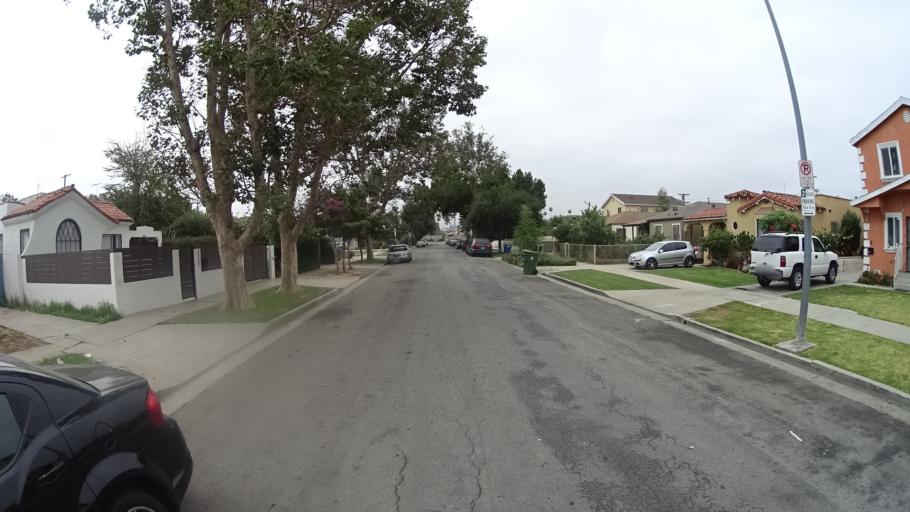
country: US
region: California
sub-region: Los Angeles County
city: View Park-Windsor Hills
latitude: 34.0246
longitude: -118.3384
